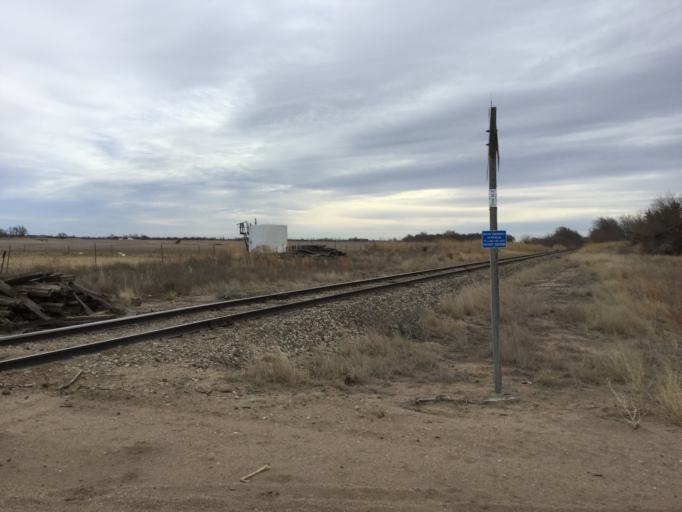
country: US
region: Kansas
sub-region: Rice County
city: Sterling
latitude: 38.1978
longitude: -98.1791
